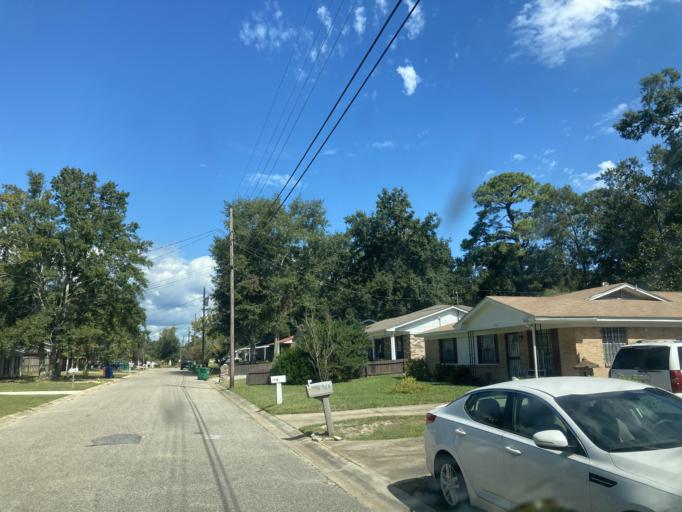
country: US
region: Mississippi
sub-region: Jackson County
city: Saint Martin
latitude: 30.4442
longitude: -88.8660
